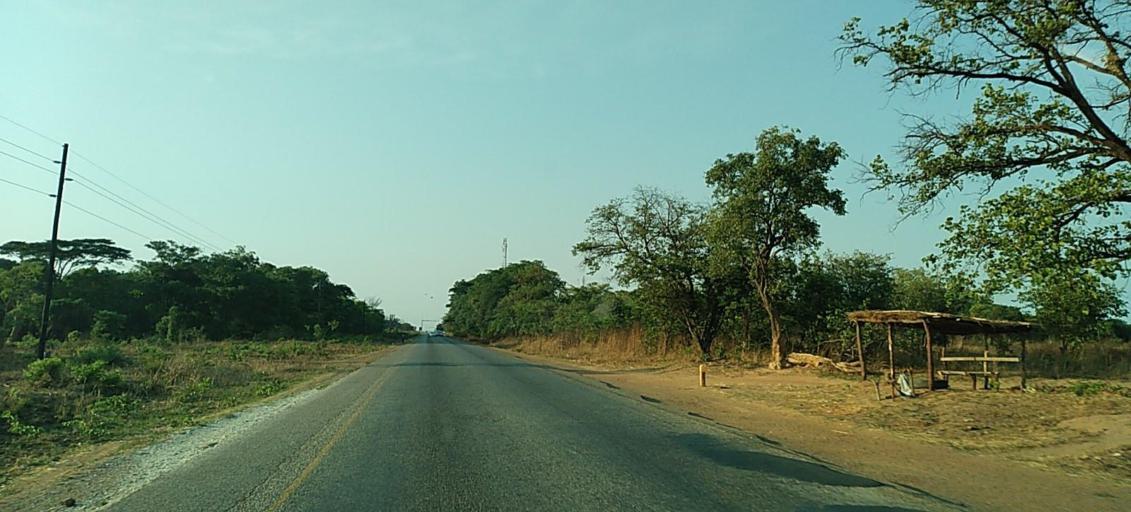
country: ZM
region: Copperbelt
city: Luanshya
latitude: -13.2384
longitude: 28.6788
